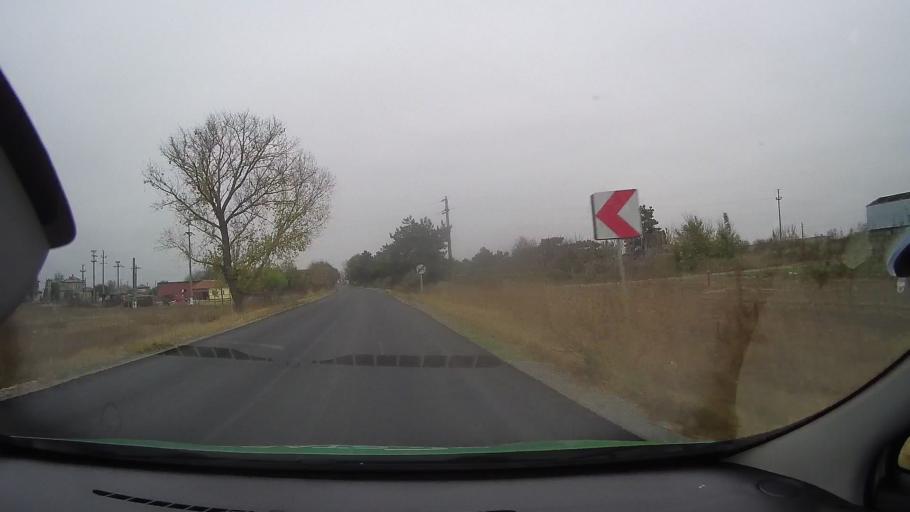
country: RO
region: Ialomita
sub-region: Comuna Valea Ciorii
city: Valea Ciorii
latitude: 44.7409
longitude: 27.5766
